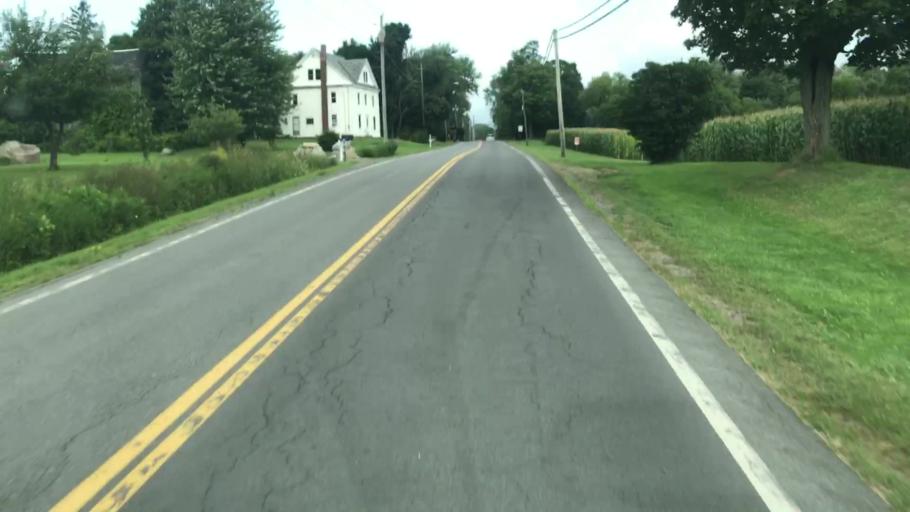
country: US
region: New York
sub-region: Cayuga County
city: Melrose Park
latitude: 42.9489
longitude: -76.5232
